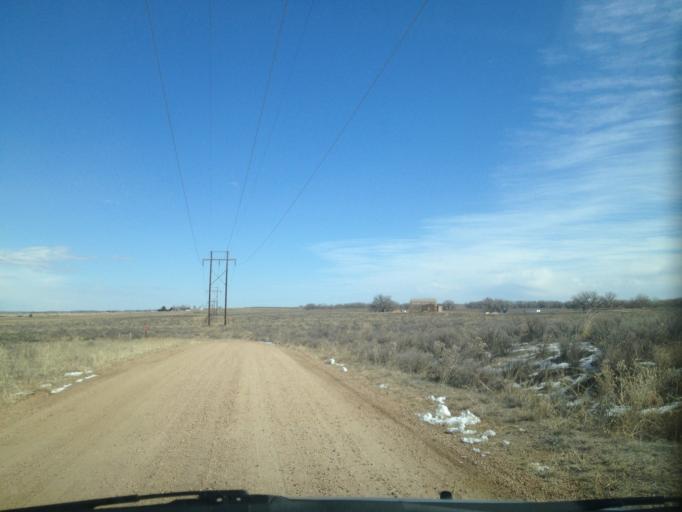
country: US
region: Colorado
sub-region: Weld County
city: Keenesburg
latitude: 40.2837
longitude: -104.2566
